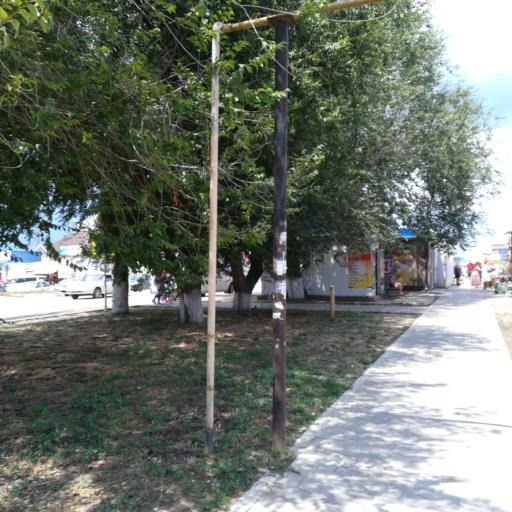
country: RU
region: Krasnodarskiy
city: Taman'
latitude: 45.2137
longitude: 36.7197
